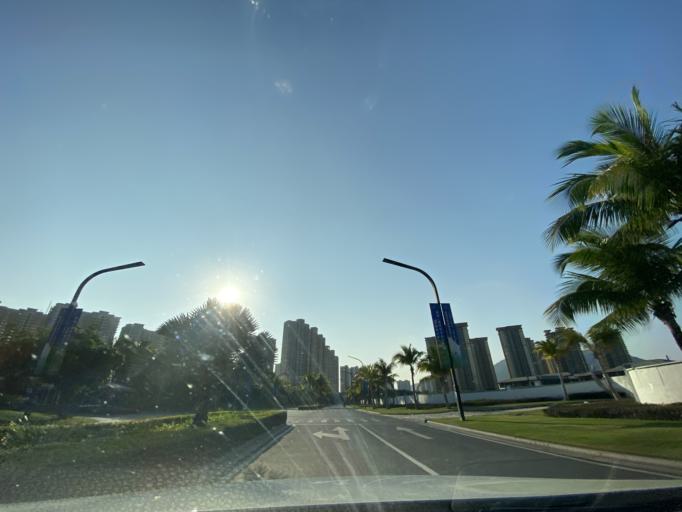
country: CN
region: Hainan
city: Xincun
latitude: 18.4219
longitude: 109.9452
